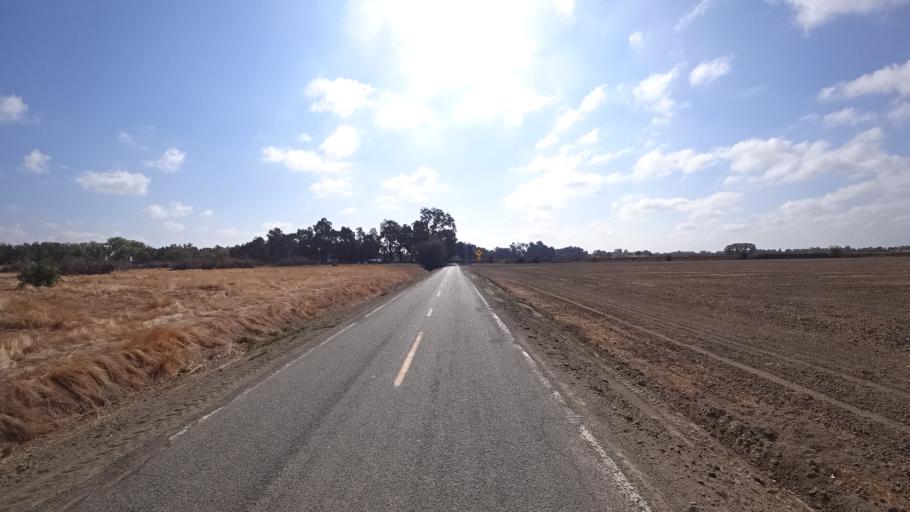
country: US
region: California
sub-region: Yolo County
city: Woodland
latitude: 38.7792
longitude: -121.6915
